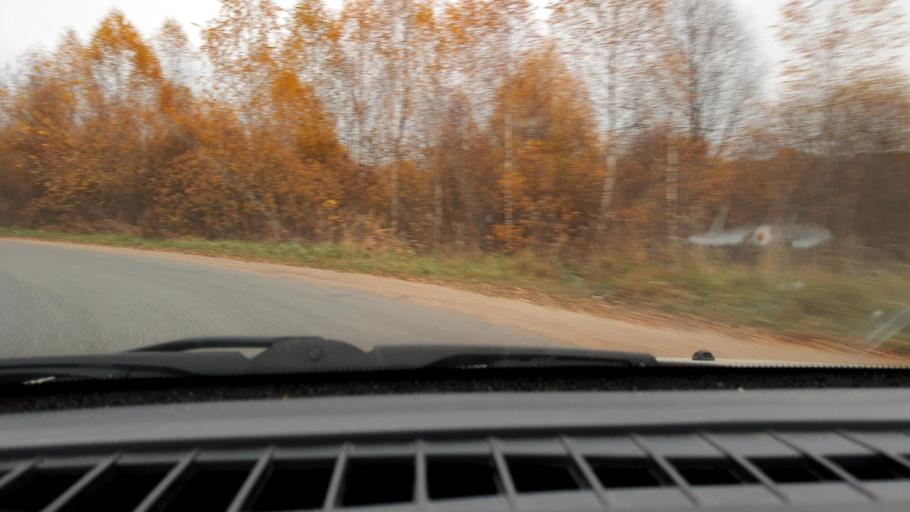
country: RU
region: Nizjnij Novgorod
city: Burevestnik
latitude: 56.0399
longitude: 43.8472
